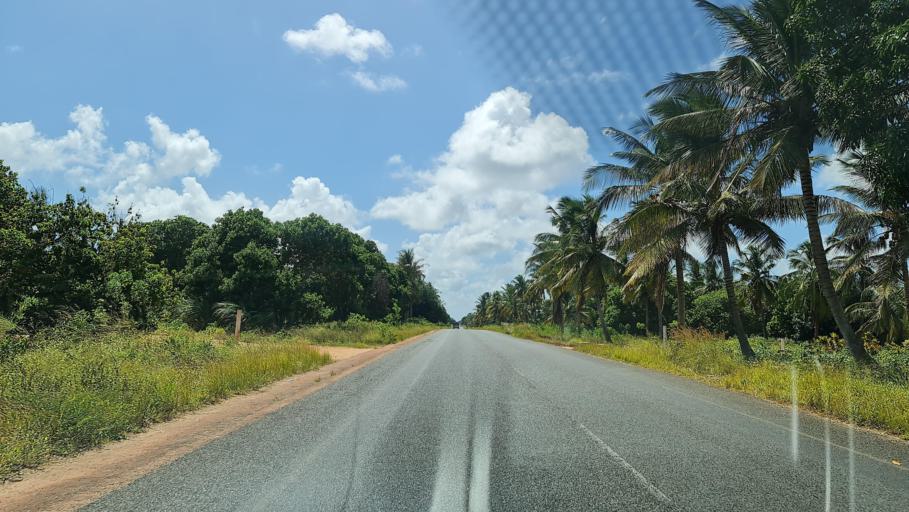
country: MZ
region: Inhambane
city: Maxixe
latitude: -24.5423
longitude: 34.8992
